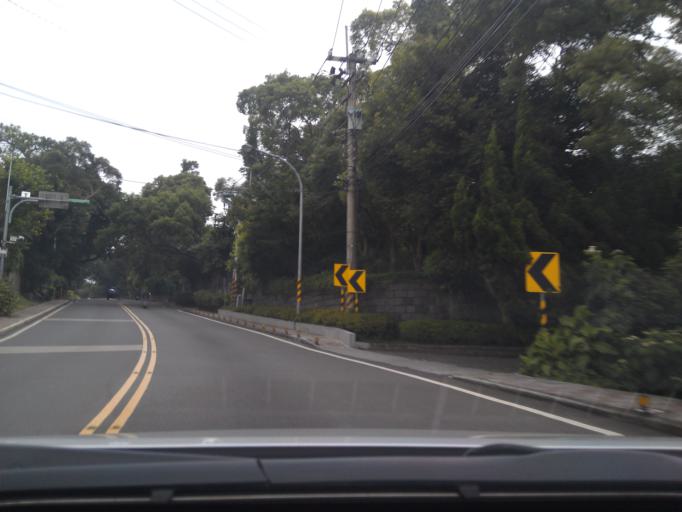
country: TW
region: Taipei
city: Taipei
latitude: 25.1206
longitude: 121.5530
